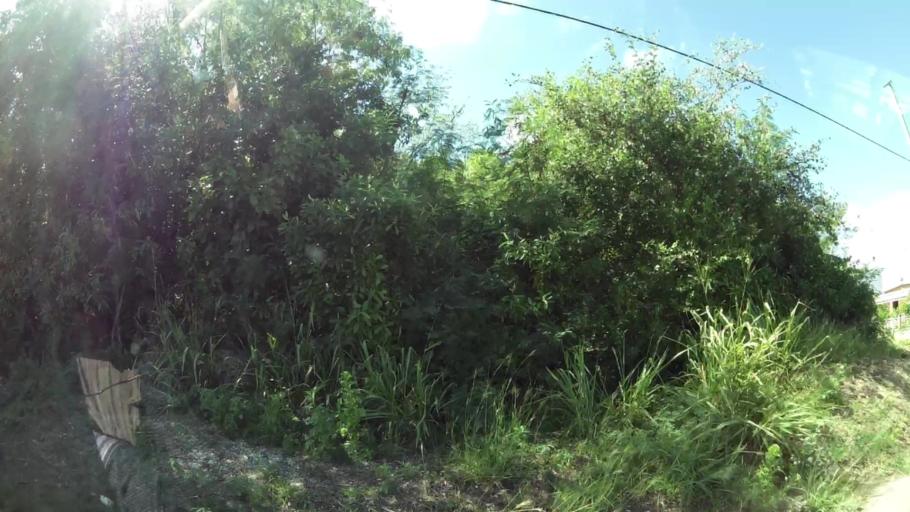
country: GP
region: Guadeloupe
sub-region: Guadeloupe
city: Petit-Canal
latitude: 16.3883
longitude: -61.4593
